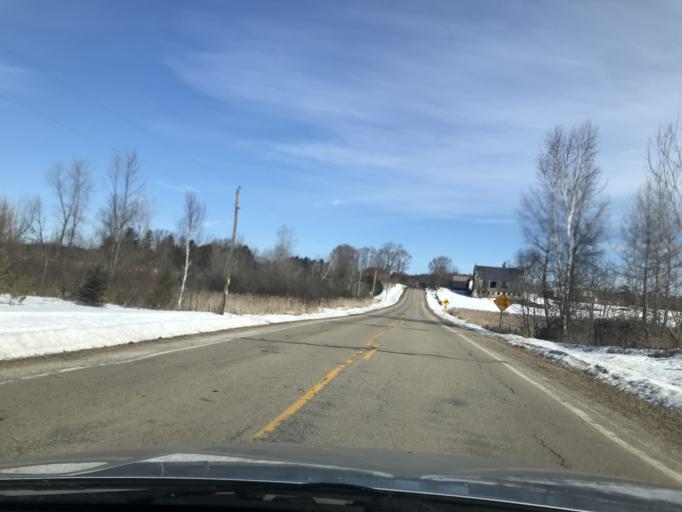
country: US
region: Wisconsin
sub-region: Oconto County
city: Gillett
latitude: 44.9579
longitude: -88.2651
